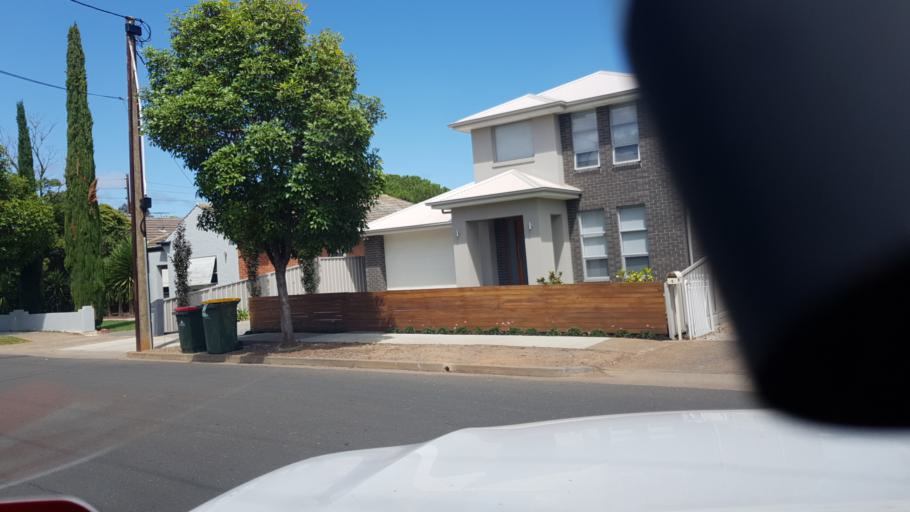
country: AU
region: South Australia
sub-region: Adelaide
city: Brighton
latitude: -35.0128
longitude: 138.5266
